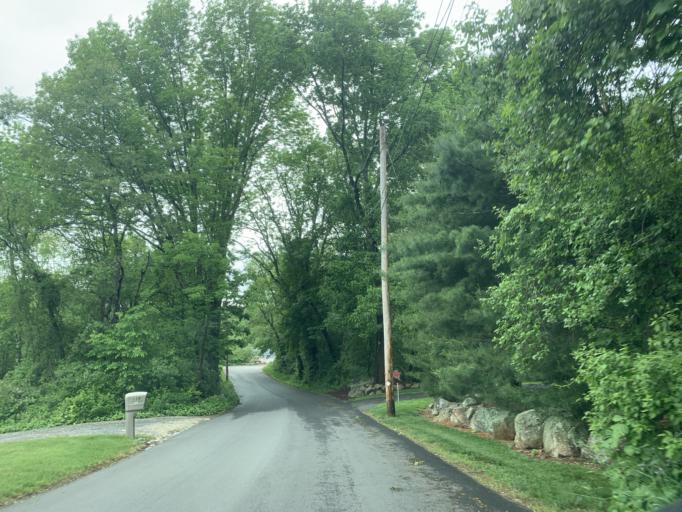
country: US
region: Massachusetts
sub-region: Worcester County
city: Upton
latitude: 42.1854
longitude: -71.6229
